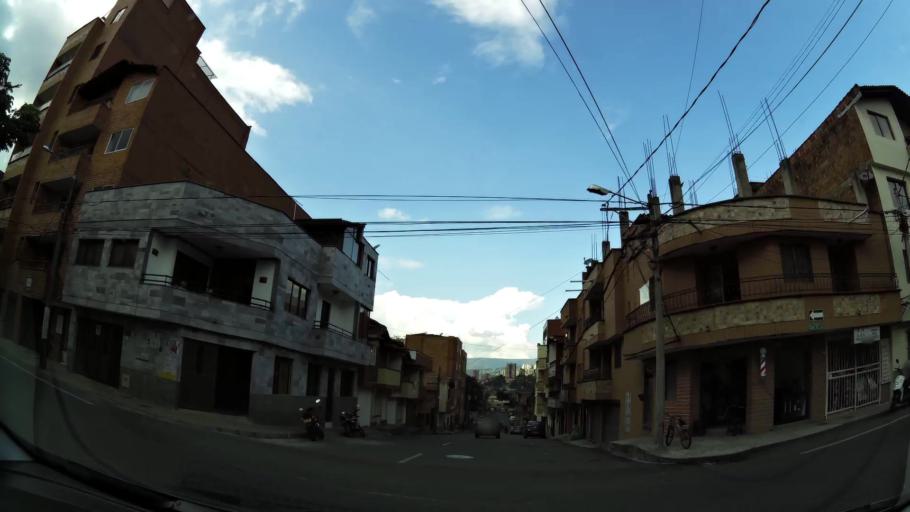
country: CO
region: Antioquia
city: Envigado
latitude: 6.1655
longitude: -75.5826
